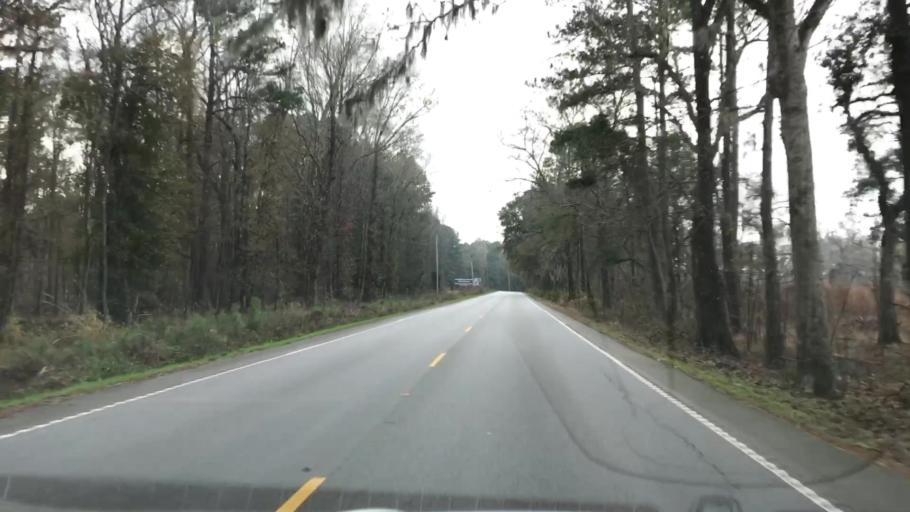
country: US
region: South Carolina
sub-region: Jasper County
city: Ridgeland
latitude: 32.5654
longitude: -80.9163
